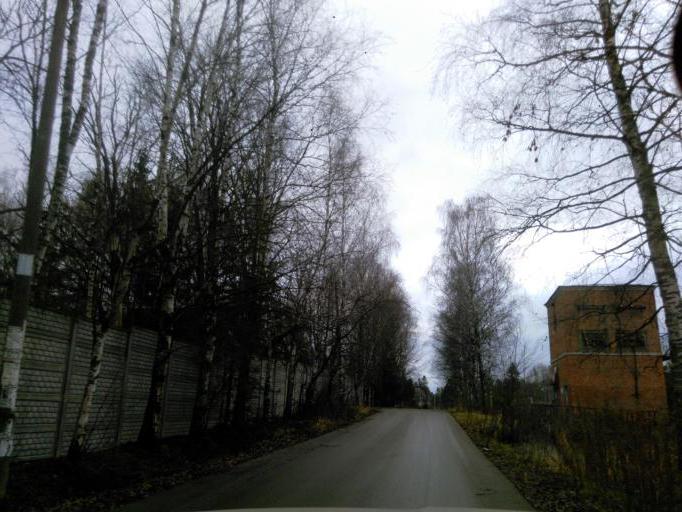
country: RU
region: Moskovskaya
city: Lozhki
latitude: 56.0556
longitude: 37.0981
